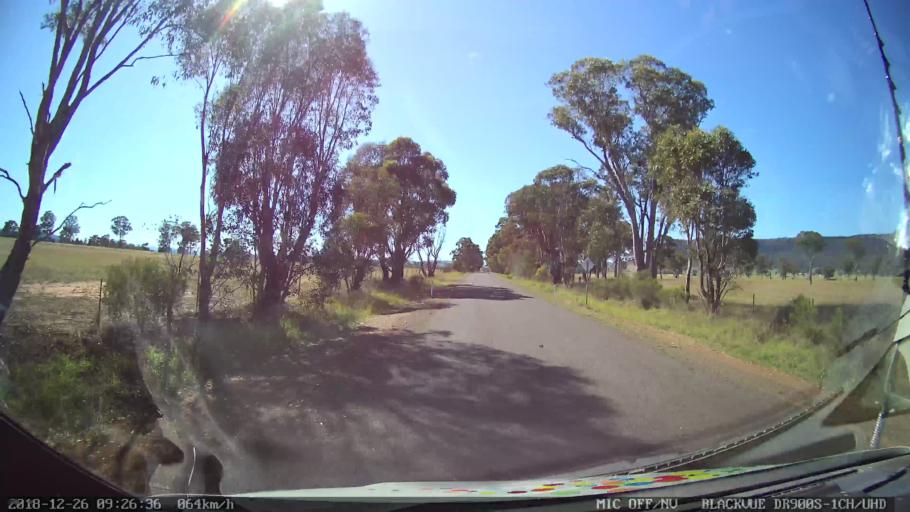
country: AU
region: New South Wales
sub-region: Mid-Western Regional
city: Kandos
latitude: -32.8295
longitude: 150.0095
